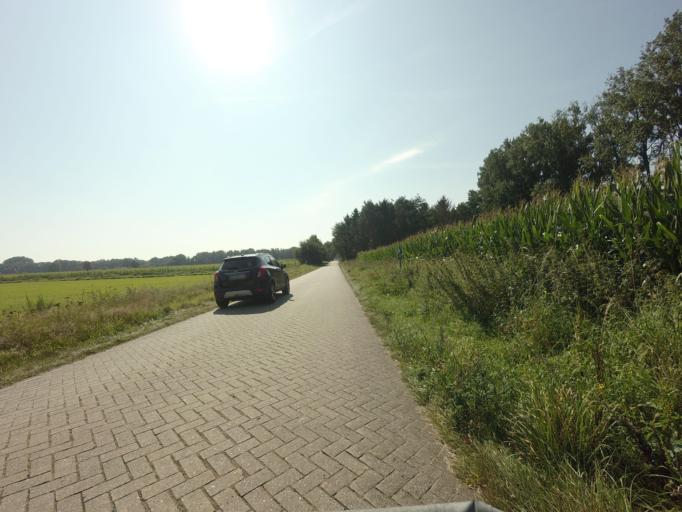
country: DE
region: Lower Saxony
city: Emlichheim
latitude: 52.5995
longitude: 6.8322
